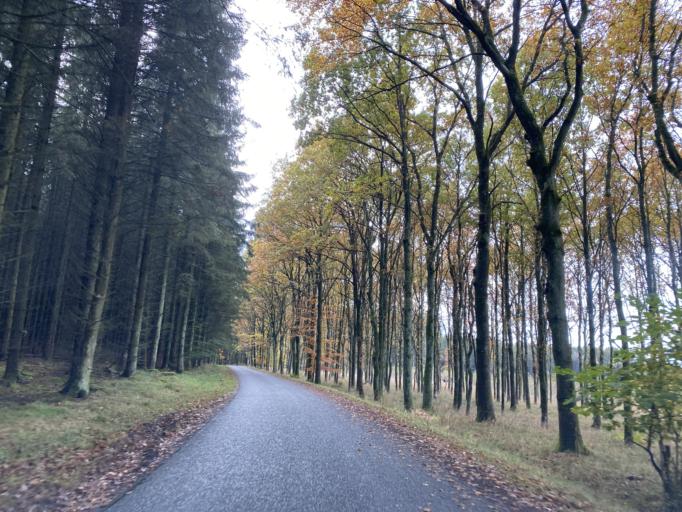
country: DK
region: Central Jutland
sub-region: Skanderborg Kommune
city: Skovby
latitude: 56.2197
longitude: 9.9501
